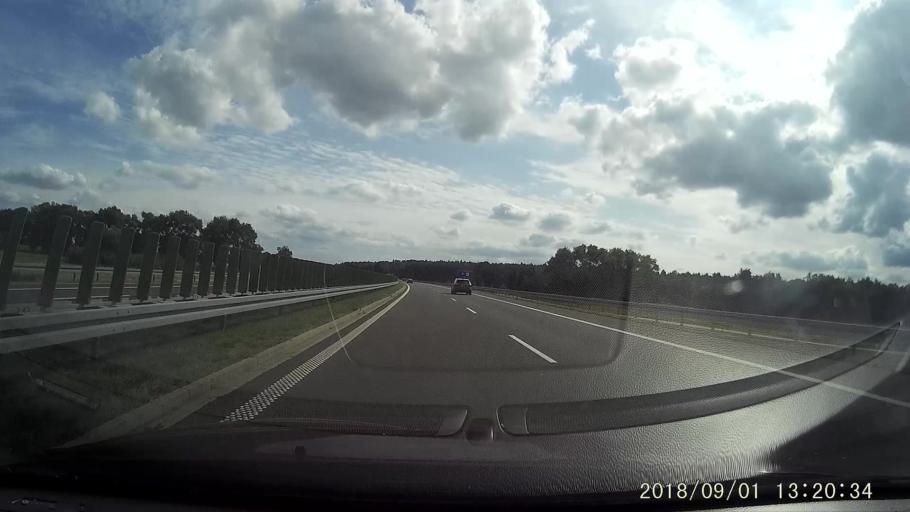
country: PL
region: West Pomeranian Voivodeship
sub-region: Powiat pyrzycki
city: Bielice
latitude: 53.1721
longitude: 14.6939
